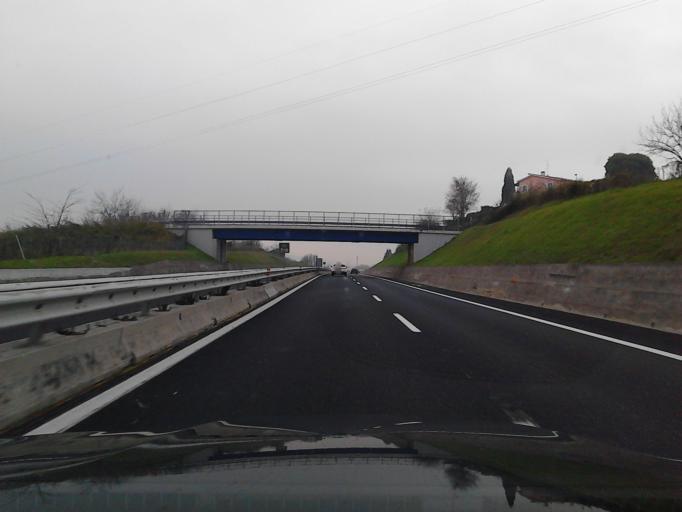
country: IT
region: Abruzzo
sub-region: Provincia di Pescara
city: San Martino Bassa
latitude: 42.5118
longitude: 14.1248
